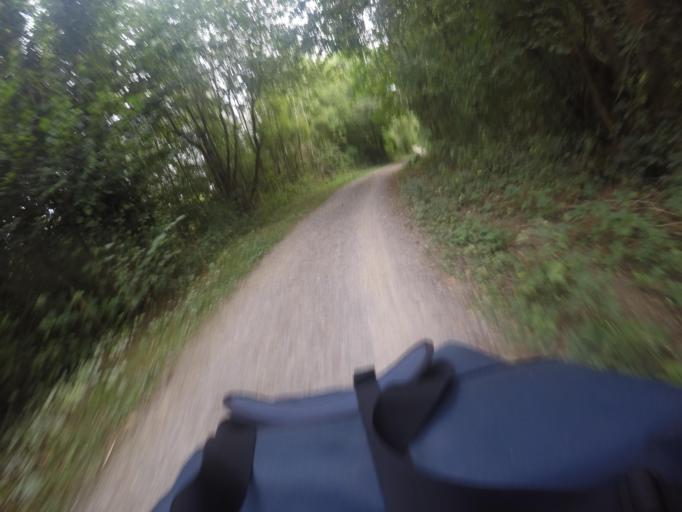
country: DE
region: North Rhine-Westphalia
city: Haan
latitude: 51.2145
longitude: 6.9998
